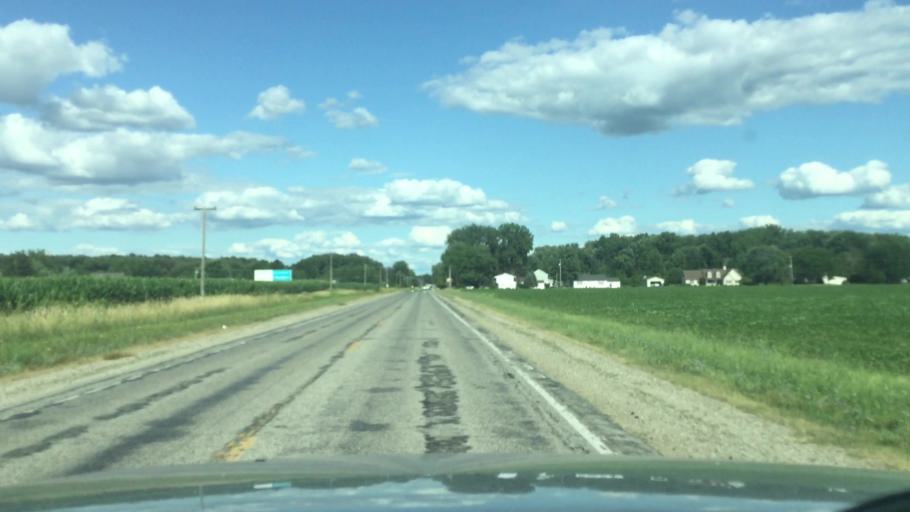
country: US
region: Michigan
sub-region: Saginaw County
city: Shields
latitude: 43.3795
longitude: -84.0766
